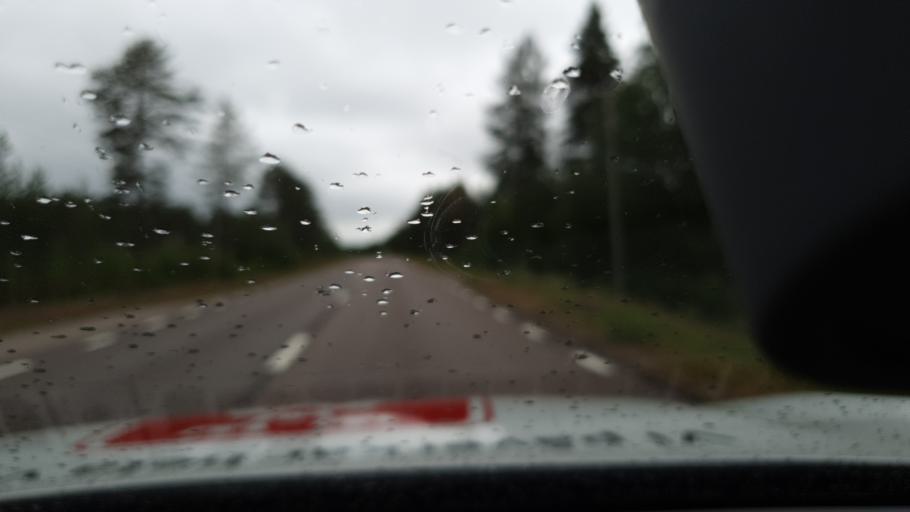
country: FI
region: Lapland
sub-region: Torniolaakso
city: Pello
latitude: 66.9907
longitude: 23.7796
